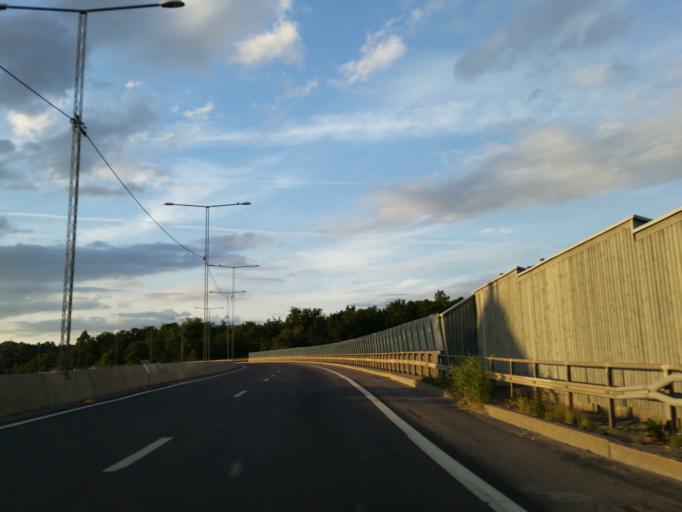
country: SE
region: Stockholm
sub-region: Stockholms Kommun
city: Bromma
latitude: 59.3662
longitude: 17.9445
